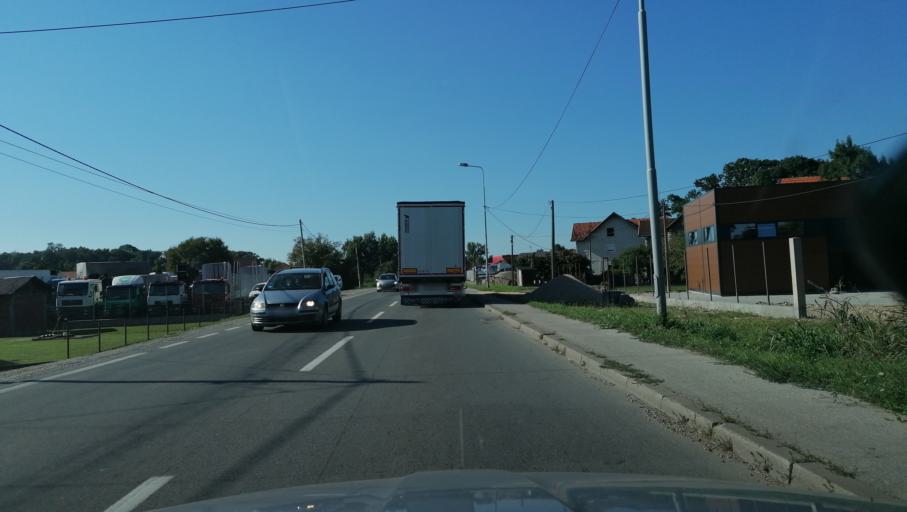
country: RS
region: Central Serbia
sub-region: Raski Okrug
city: Kraljevo
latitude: 43.7505
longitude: 20.6613
